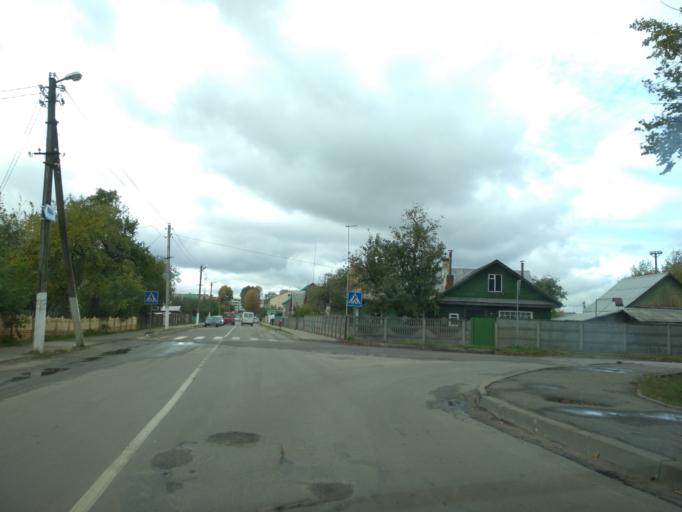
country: BY
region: Minsk
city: Mar''ina Horka
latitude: 53.5164
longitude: 28.1541
